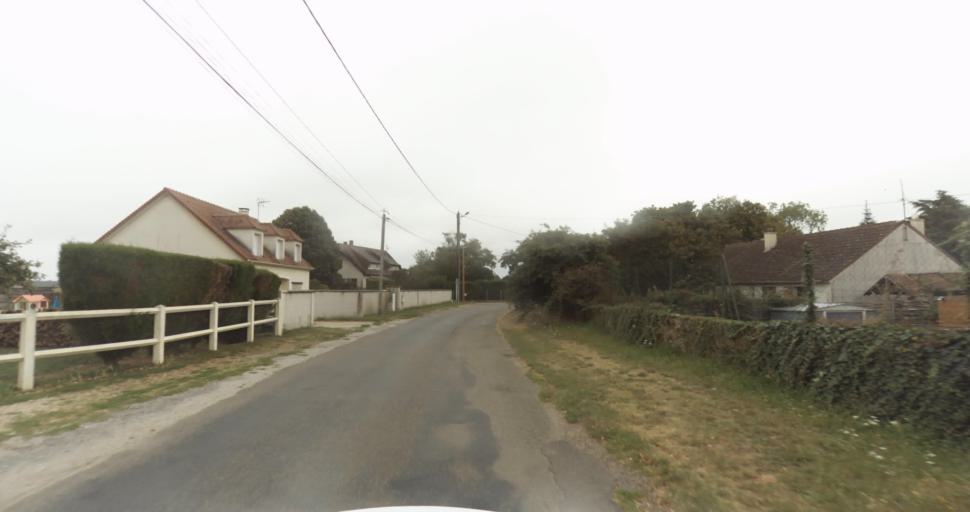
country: FR
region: Centre
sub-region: Departement d'Eure-et-Loir
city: Vert-en-Drouais
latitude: 48.7710
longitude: 1.2900
